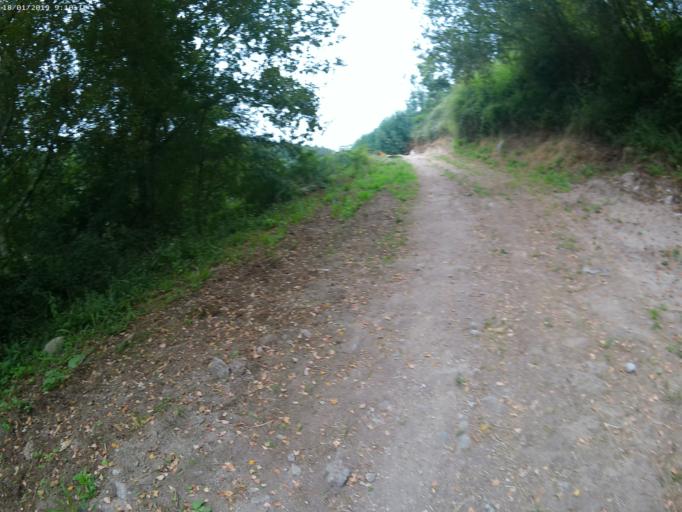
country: PT
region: Viana do Castelo
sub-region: Ponte da Barca
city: Ponte da Barca
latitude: 41.8064
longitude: -8.4503
